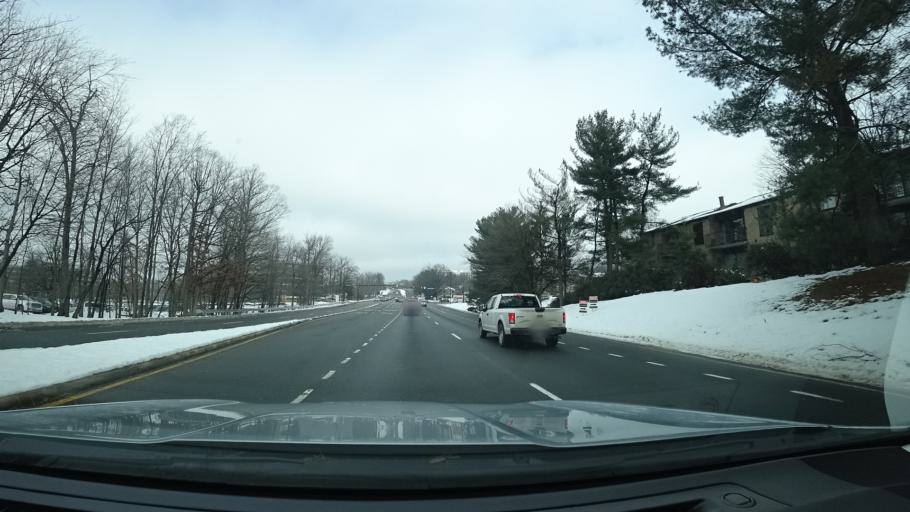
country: US
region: Virginia
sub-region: Fairfax County
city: Reston
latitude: 38.9446
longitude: -77.3601
